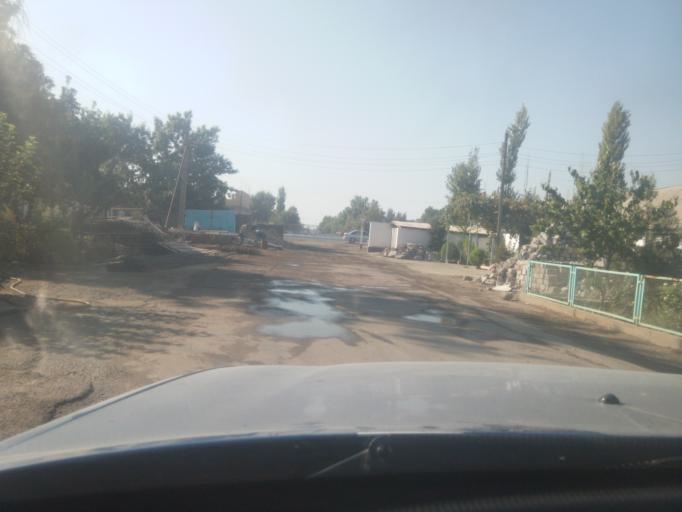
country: UZ
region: Sirdaryo
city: Guliston
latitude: 40.4937
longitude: 68.7850
